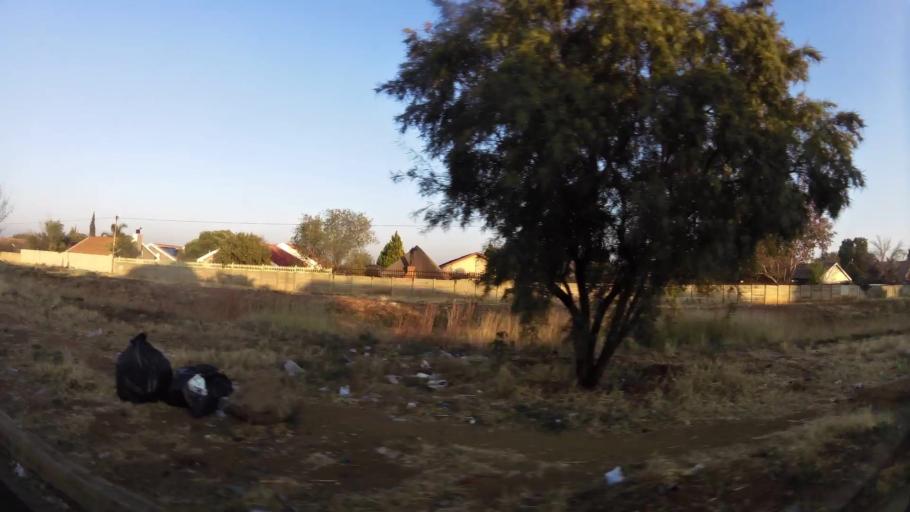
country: ZA
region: Orange Free State
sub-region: Mangaung Metropolitan Municipality
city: Bloemfontein
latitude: -29.1004
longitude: 26.1634
